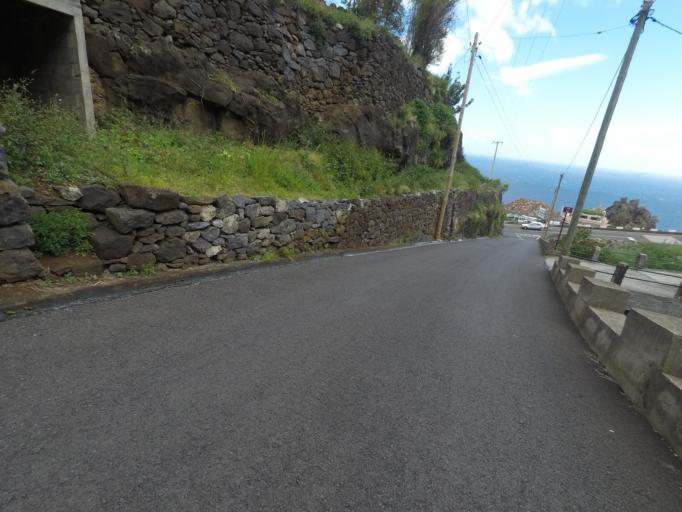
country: PT
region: Madeira
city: Calheta
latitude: 32.7252
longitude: -17.1776
